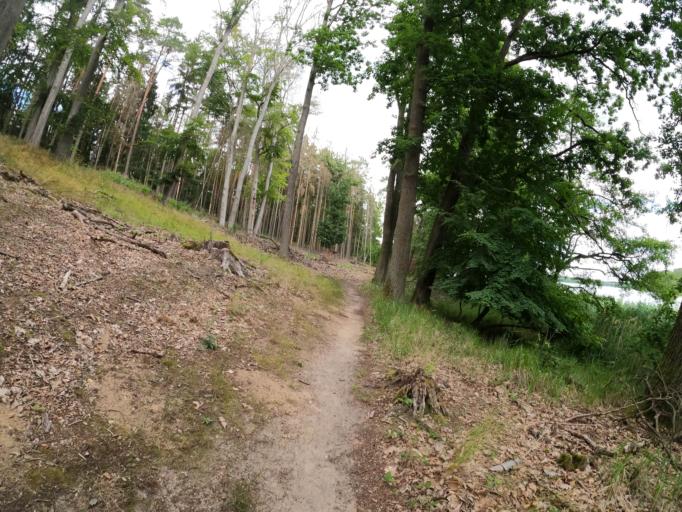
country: DE
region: Brandenburg
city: Angermunde
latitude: 53.0244
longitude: 13.9169
